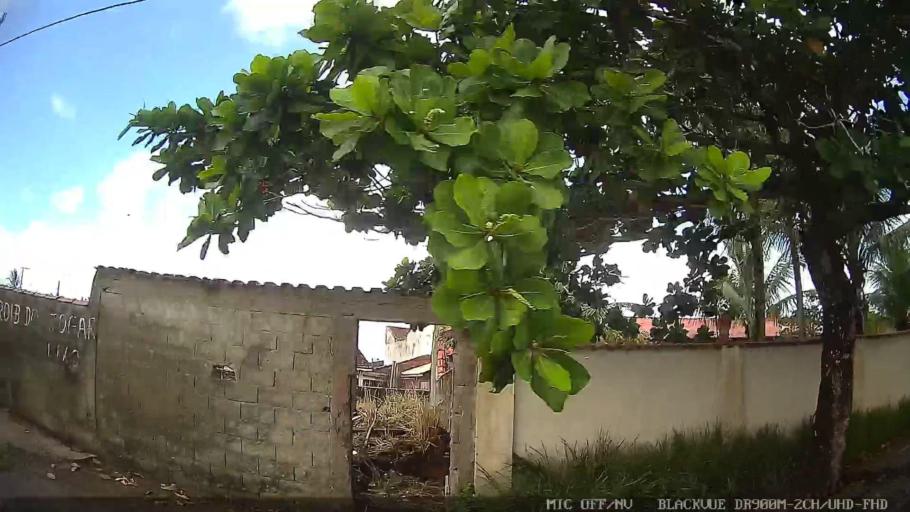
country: BR
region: Sao Paulo
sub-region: Itanhaem
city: Itanhaem
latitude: -24.2303
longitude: -46.8694
